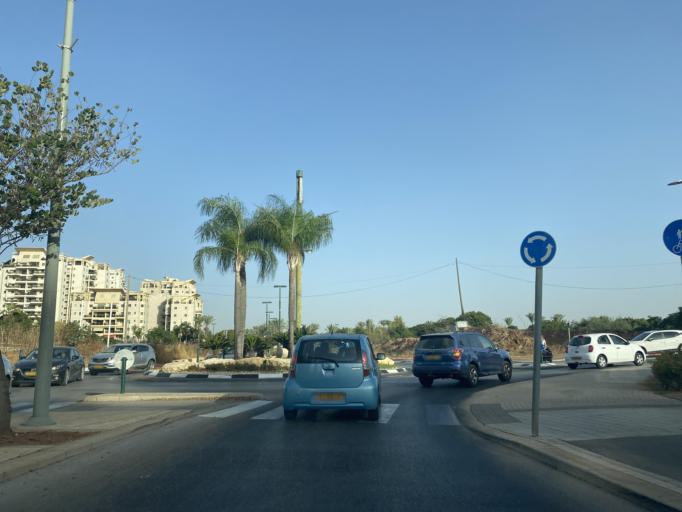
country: IL
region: Central District
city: Kfar Saba
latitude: 32.1642
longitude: 34.9059
